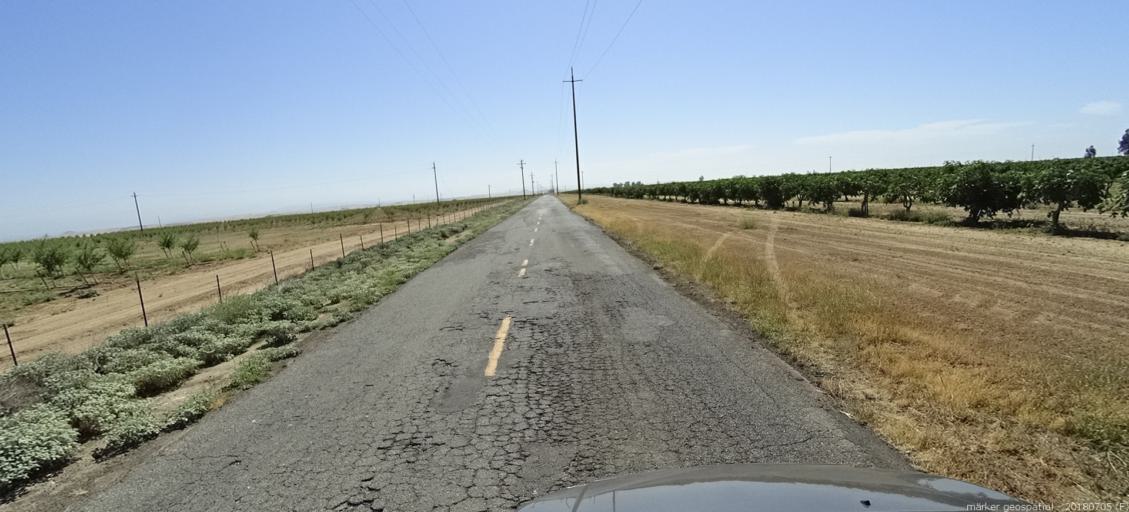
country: US
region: California
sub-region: Madera County
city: Fairmead
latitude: 37.1268
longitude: -120.0999
